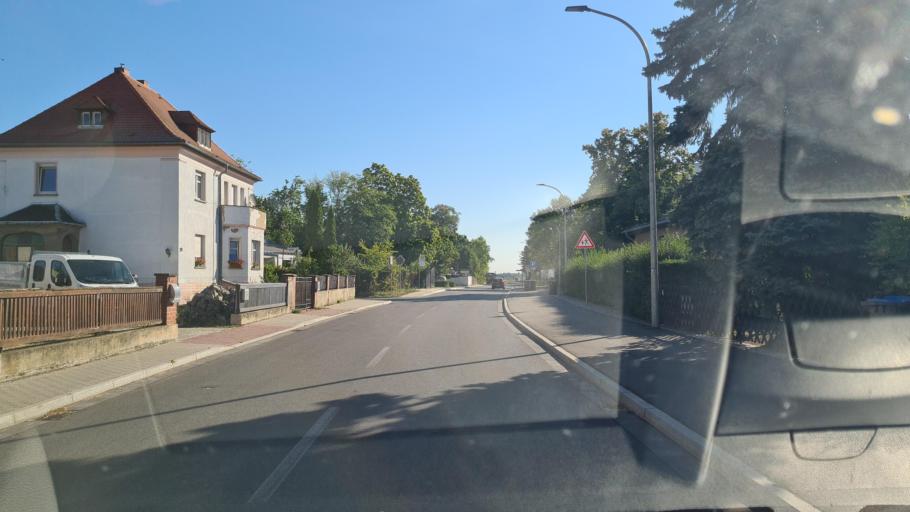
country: DE
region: Saxony
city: Borna
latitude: 51.1283
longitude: 12.5073
